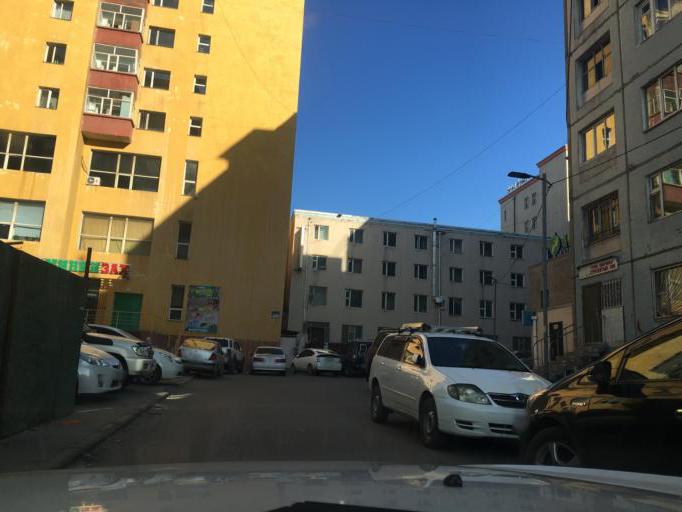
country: MN
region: Ulaanbaatar
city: Ulaanbaatar
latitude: 47.9215
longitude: 106.8670
